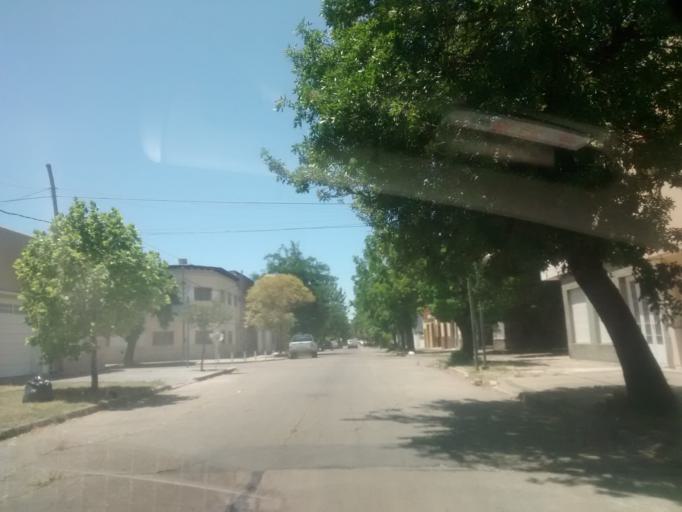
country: AR
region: Buenos Aires
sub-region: Partido de La Plata
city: La Plata
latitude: -34.9403
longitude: -57.9482
